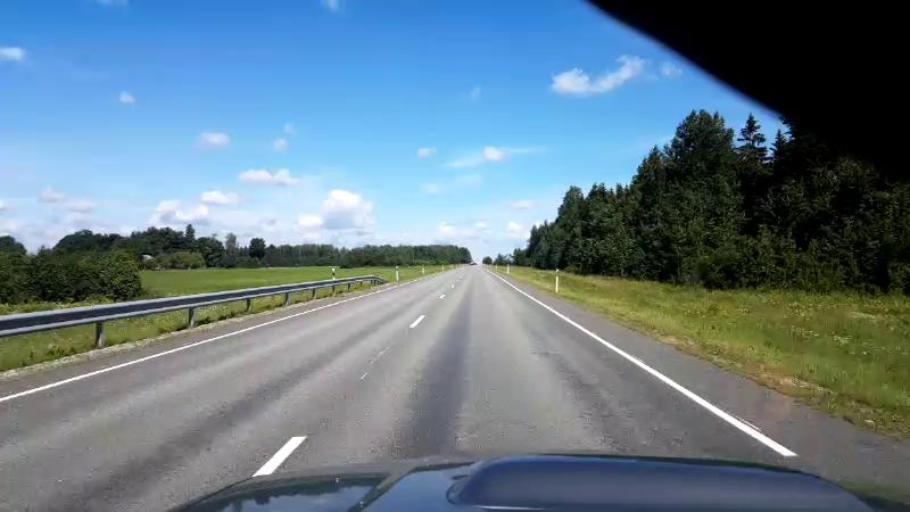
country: EE
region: Jaervamaa
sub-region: Jaerva-Jaani vald
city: Jarva-Jaani
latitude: 59.1570
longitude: 25.7654
